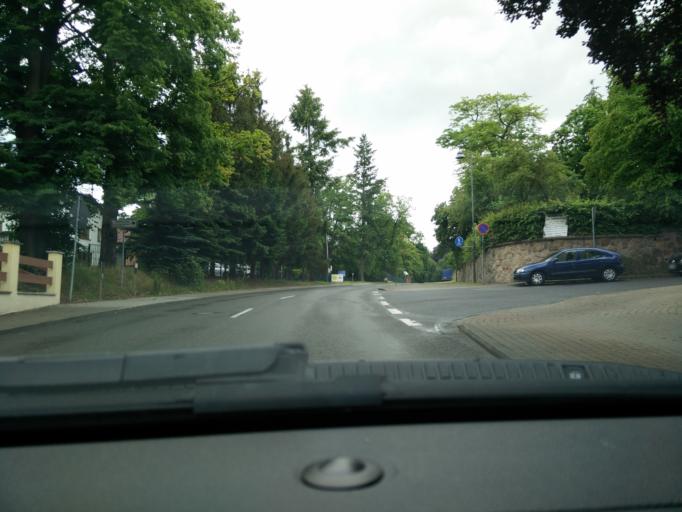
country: DE
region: Saxony
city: Grimma
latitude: 51.2297
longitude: 12.7239
